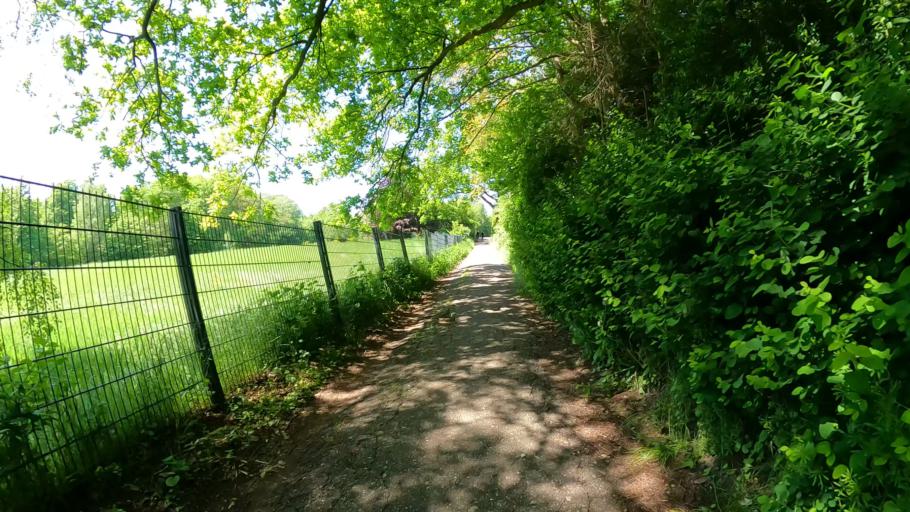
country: DE
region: Hamburg
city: Harburg
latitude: 53.4541
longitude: 9.9516
